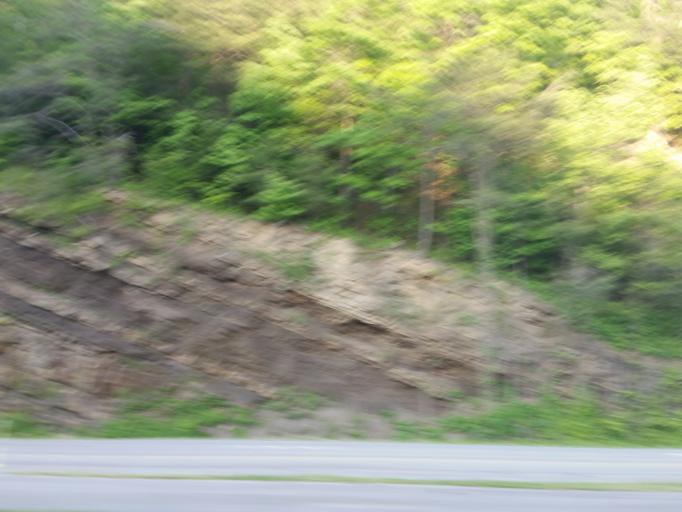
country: US
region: Virginia
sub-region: Russell County
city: Lebanon
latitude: 36.7773
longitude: -82.0815
